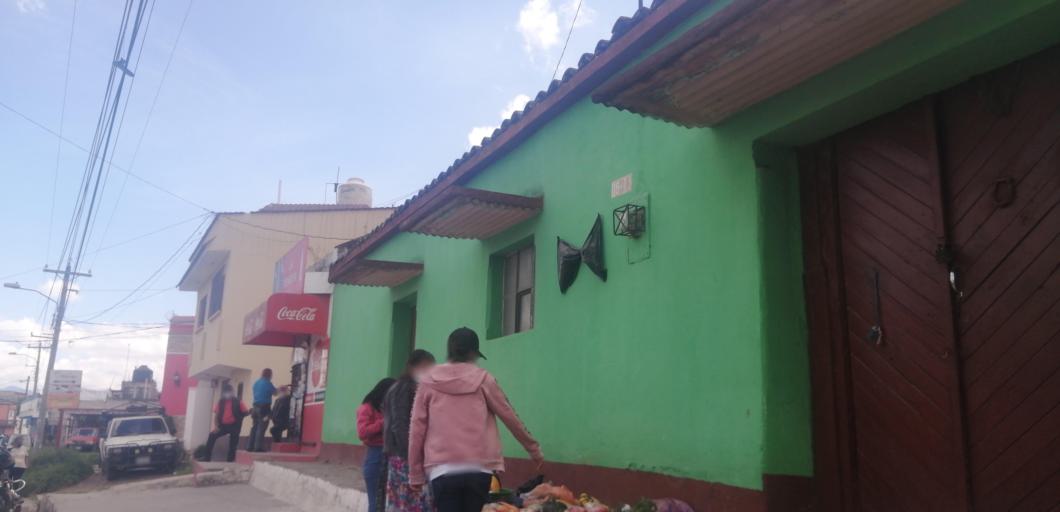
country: GT
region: Quetzaltenango
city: Quetzaltenango
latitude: 14.8320
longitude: -91.5308
